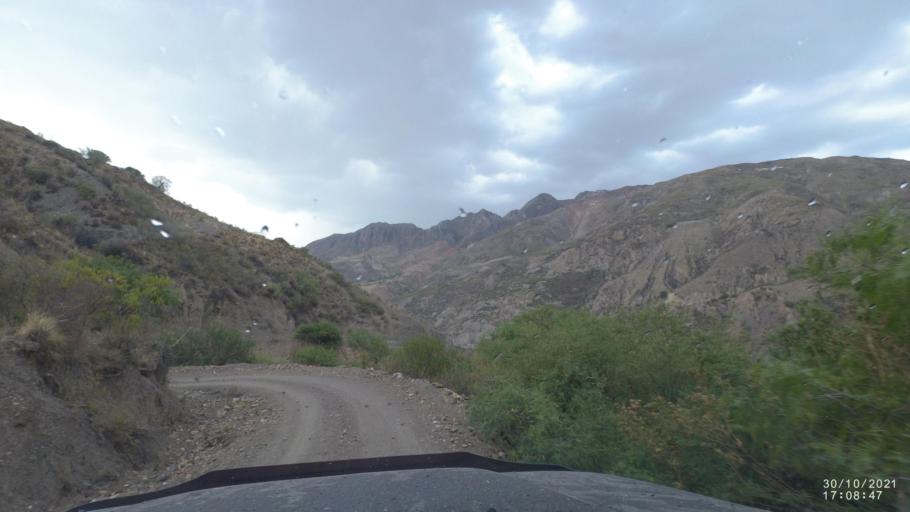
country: BO
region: Cochabamba
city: Colchani
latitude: -17.5606
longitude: -66.6240
